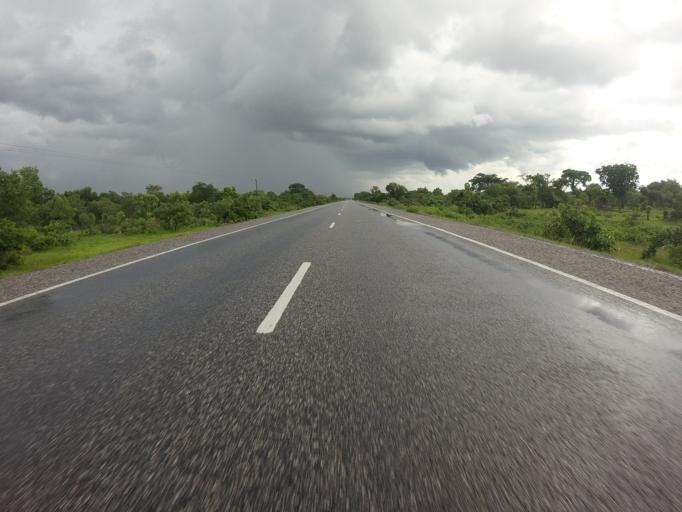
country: GH
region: Northern
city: Tamale
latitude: 9.1585
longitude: -1.5230
